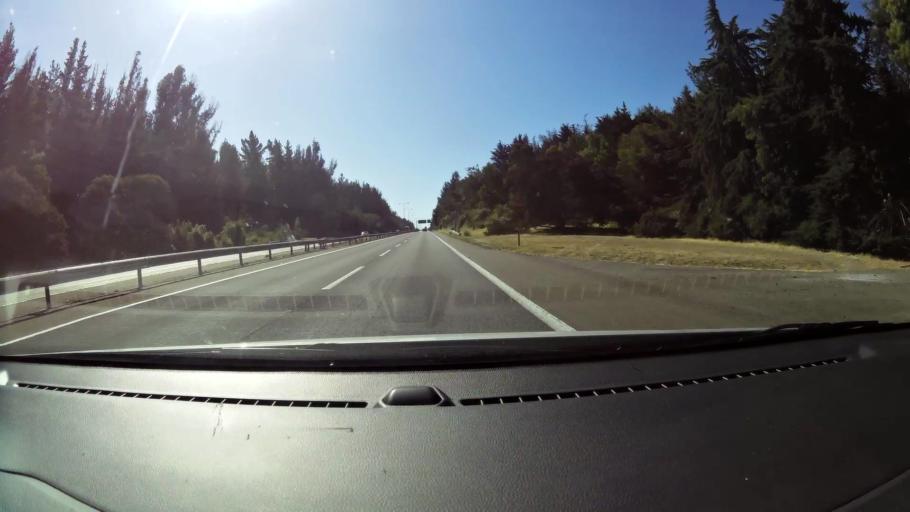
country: CL
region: Valparaiso
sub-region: Provincia de Valparaiso
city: Vina del Mar
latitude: -33.1660
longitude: -71.5326
